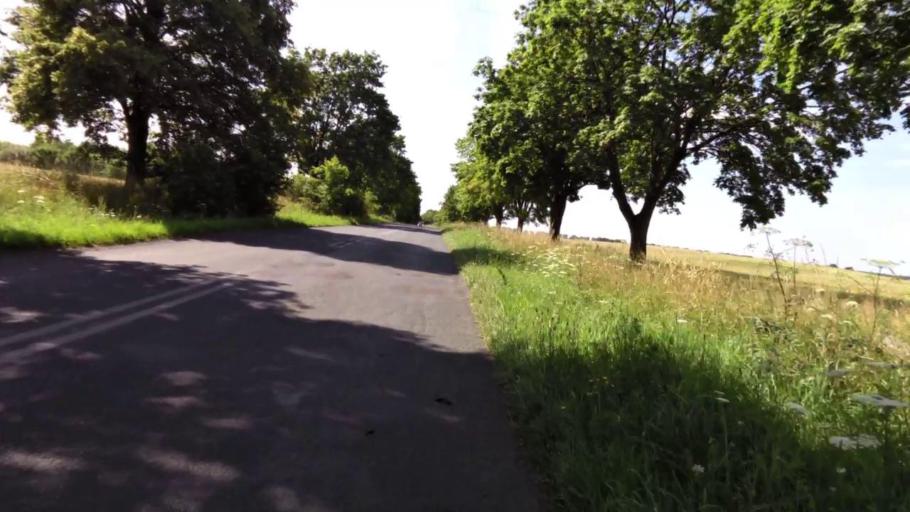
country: PL
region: West Pomeranian Voivodeship
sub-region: Powiat stargardzki
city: Dobrzany
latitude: 53.3996
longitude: 15.4309
